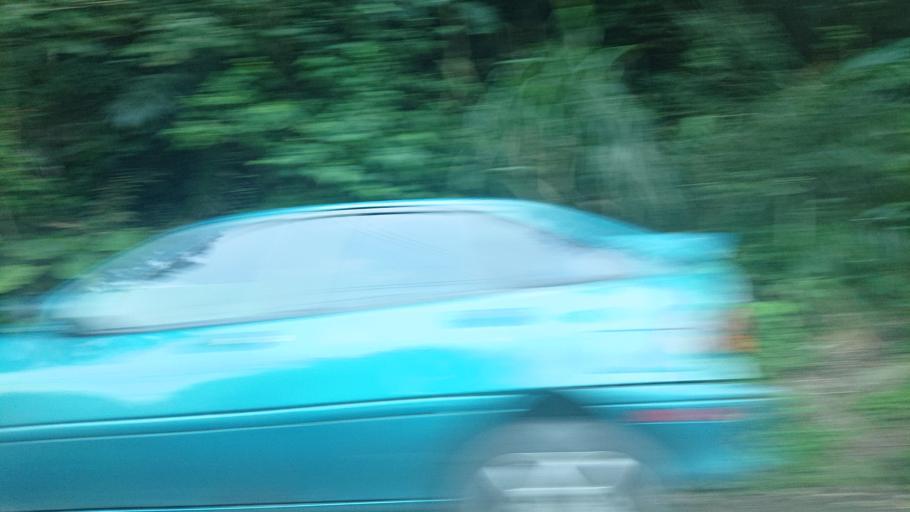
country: TW
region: Taiwan
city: Daxi
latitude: 24.8868
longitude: 121.3769
